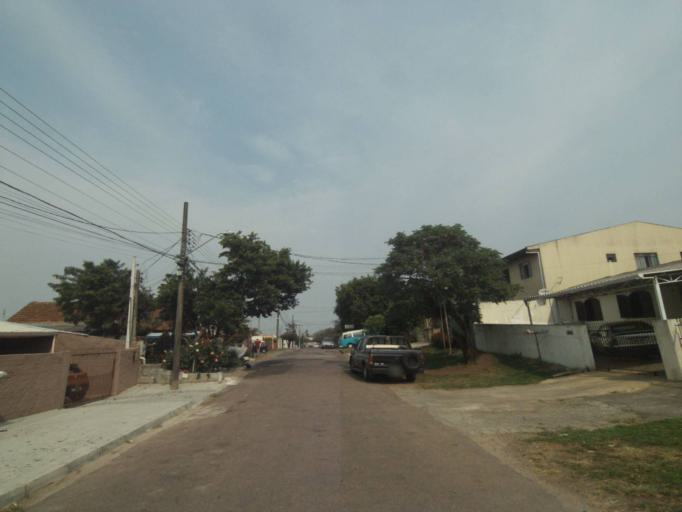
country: BR
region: Parana
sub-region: Sao Jose Dos Pinhais
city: Sao Jose dos Pinhais
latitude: -25.5261
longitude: -49.2722
